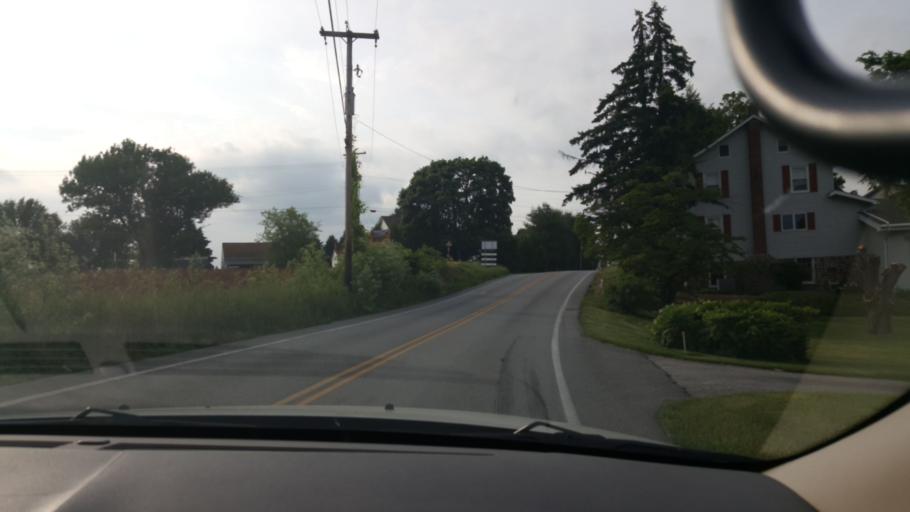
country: US
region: Pennsylvania
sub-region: York County
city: Shiloh
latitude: 40.0042
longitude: -76.8026
